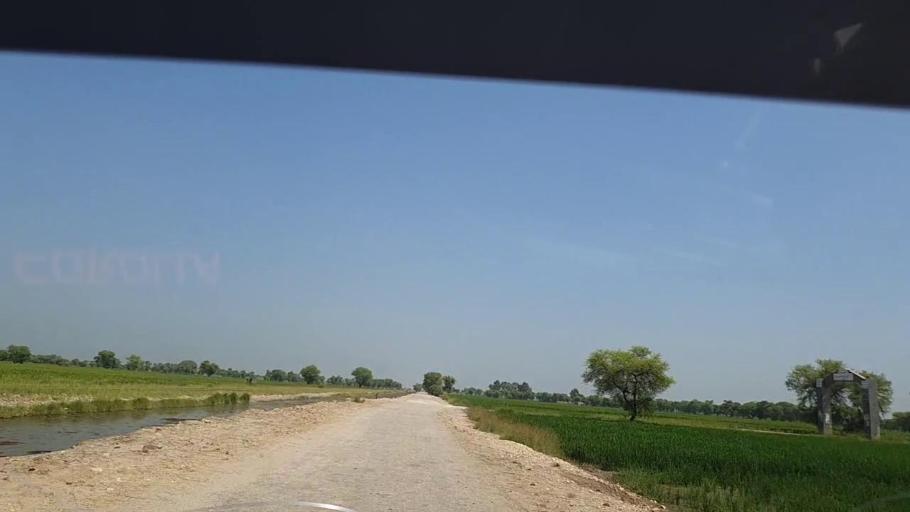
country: PK
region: Sindh
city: Tangwani
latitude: 28.2836
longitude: 69.0259
